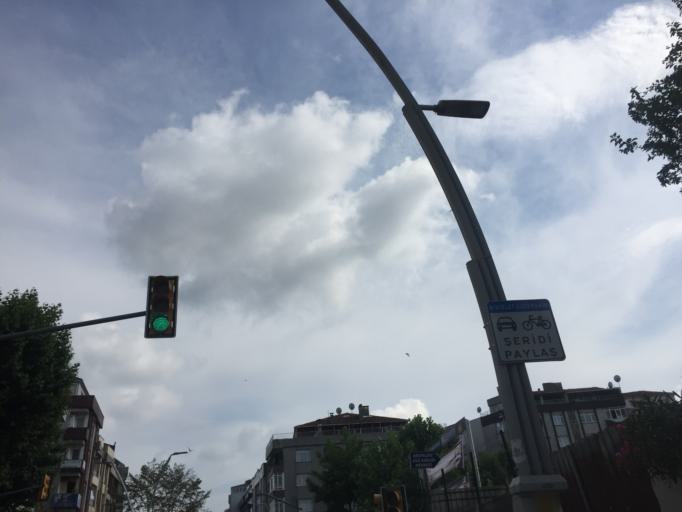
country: TR
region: Istanbul
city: Zeytinburnu
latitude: 41.0017
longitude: 28.9043
